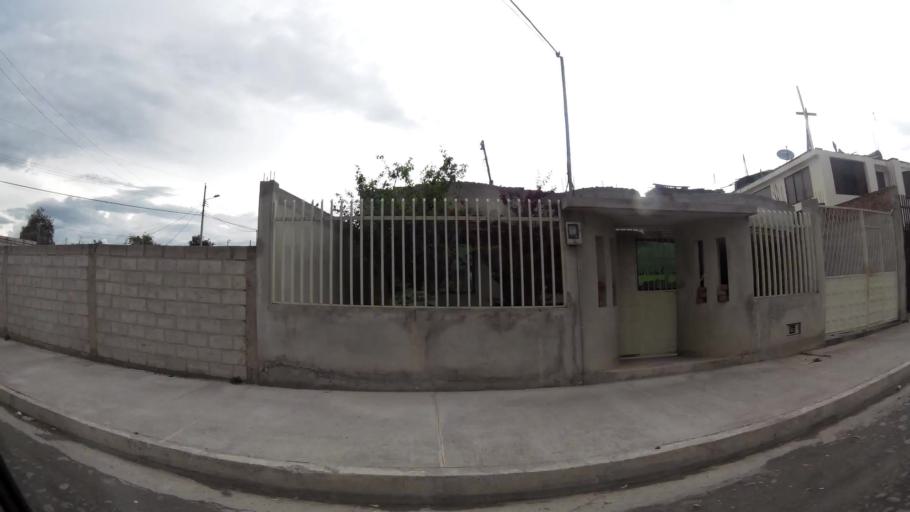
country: EC
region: Tungurahua
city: Ambato
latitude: -1.2792
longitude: -78.6227
